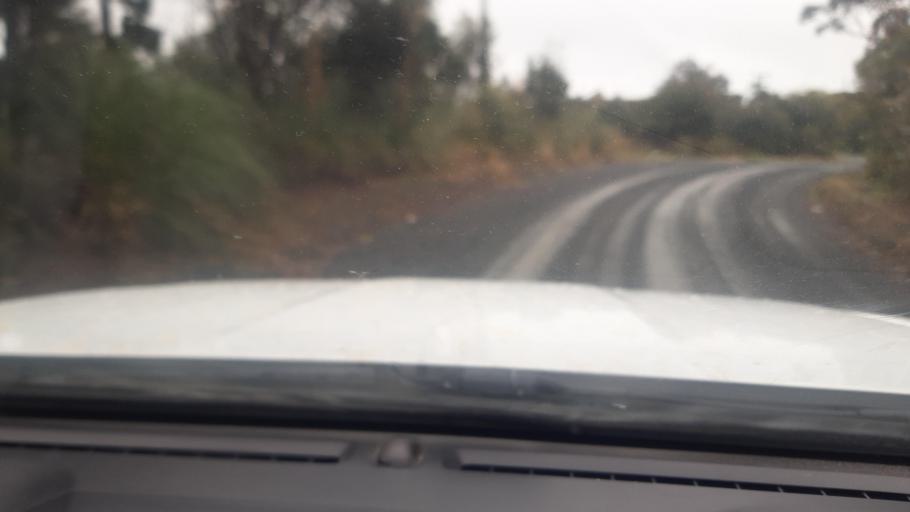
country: NZ
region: Northland
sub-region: Far North District
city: Kaitaia
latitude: -34.9897
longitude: 173.2132
